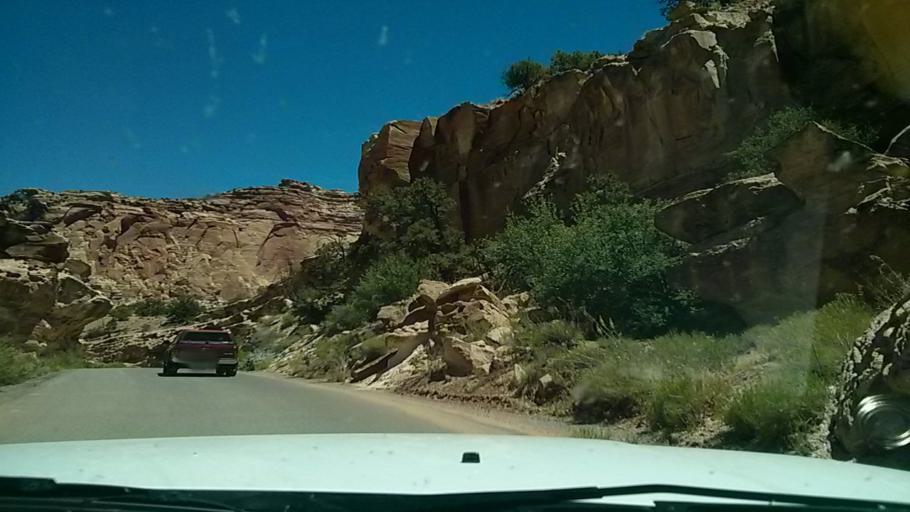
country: US
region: Utah
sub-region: Wayne County
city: Loa
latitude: 38.2078
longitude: -111.1998
